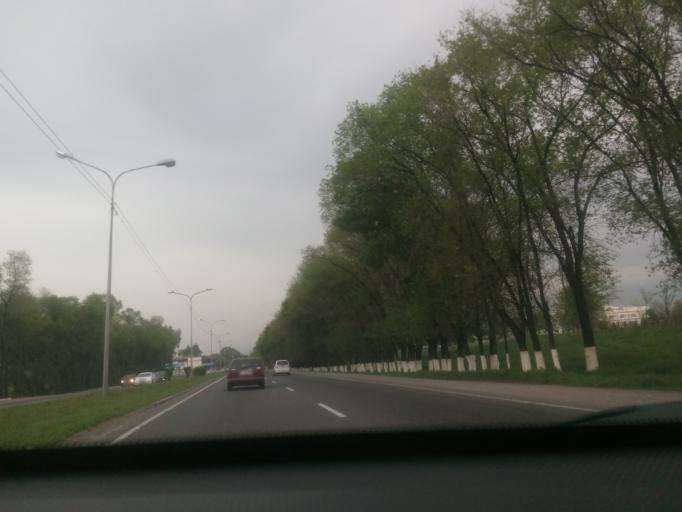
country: KZ
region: Almaty Oblysy
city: Burunday
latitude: 43.2253
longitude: 76.7295
